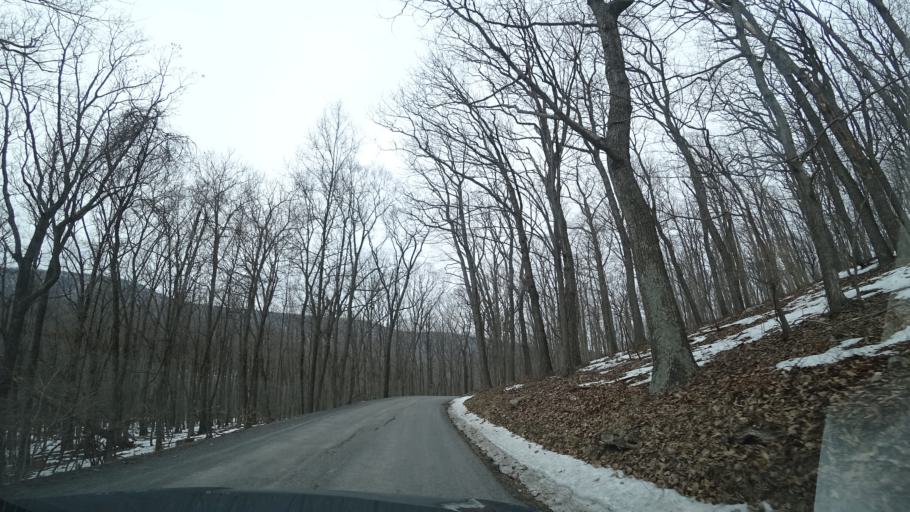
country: US
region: Virginia
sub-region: Shenandoah County
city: Basye
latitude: 38.9271
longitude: -78.6900
